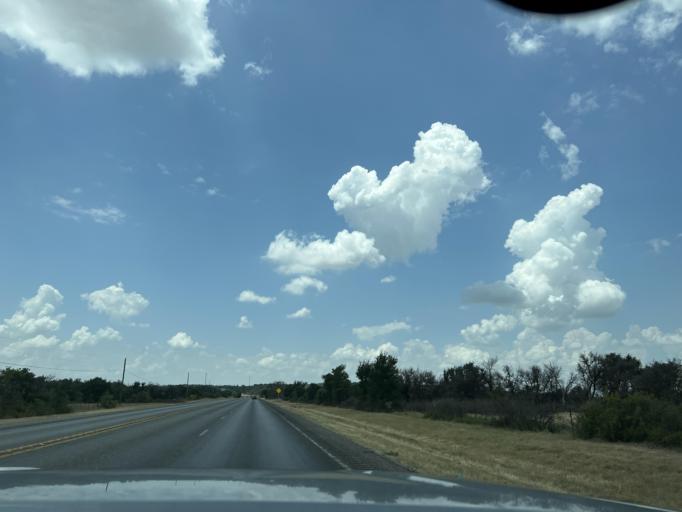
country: US
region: Texas
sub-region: Parker County
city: Springtown
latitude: 32.9298
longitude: -97.7043
